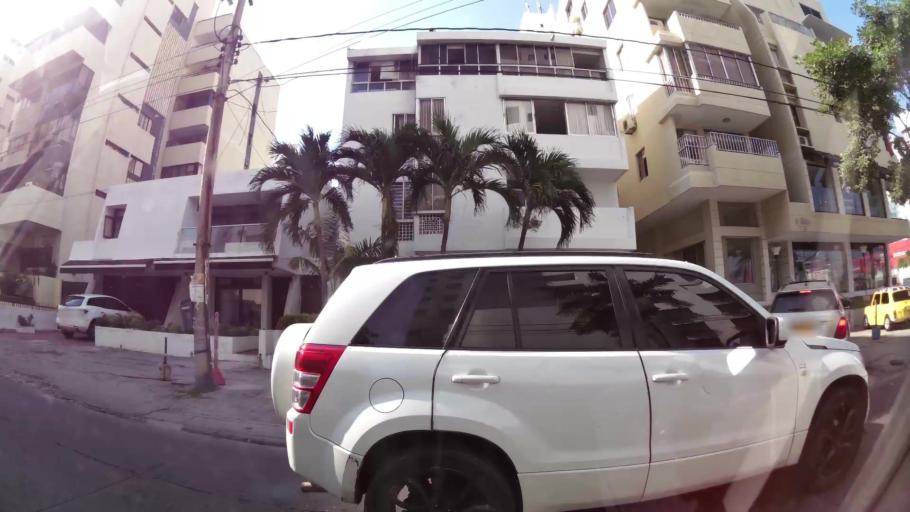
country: CO
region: Bolivar
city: Cartagena
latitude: 10.4060
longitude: -75.5516
